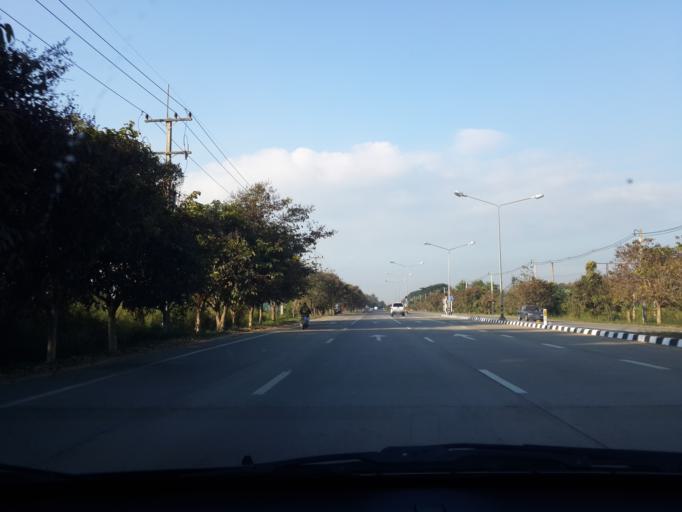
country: TH
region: Chiang Mai
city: San Sai
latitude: 18.8596
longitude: 99.1077
